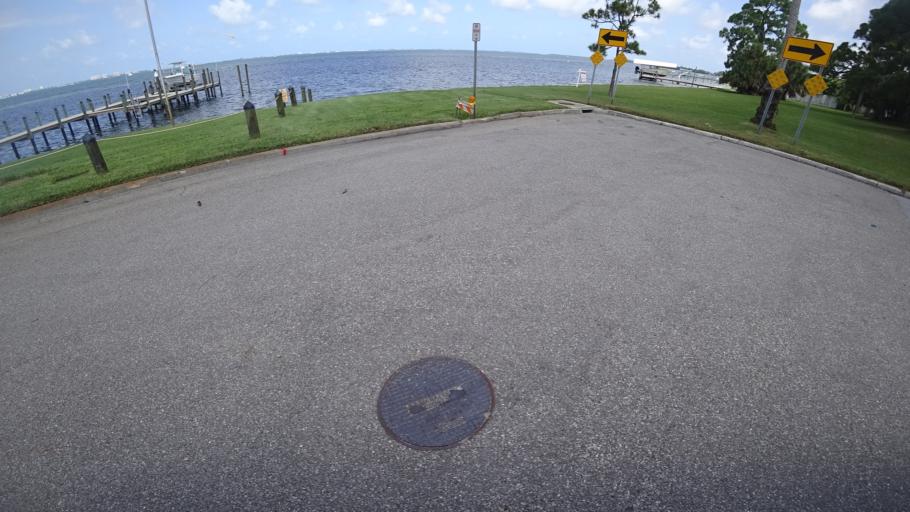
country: US
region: Florida
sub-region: Manatee County
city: Whitfield
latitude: 27.4013
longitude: -82.5707
